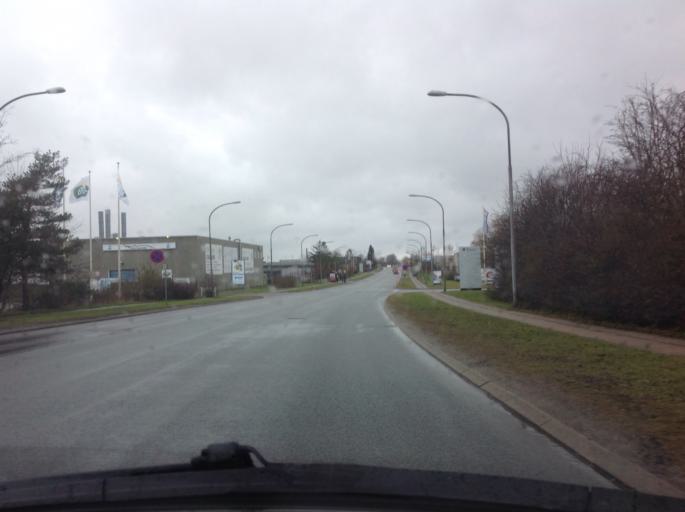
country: DK
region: Capital Region
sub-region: Ishoj Kommune
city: Ishoj
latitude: 55.6169
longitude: 12.3236
